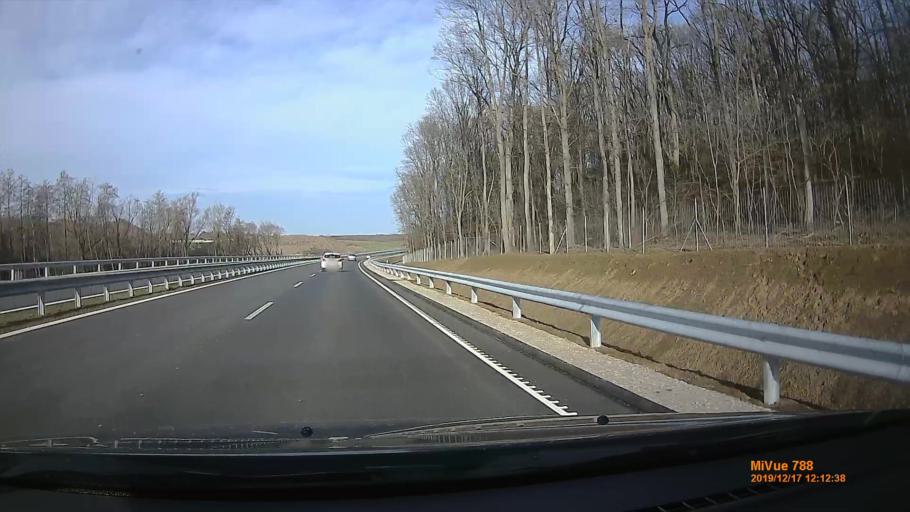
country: HU
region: Somogy
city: Kaposvar
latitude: 46.4447
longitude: 17.7695
